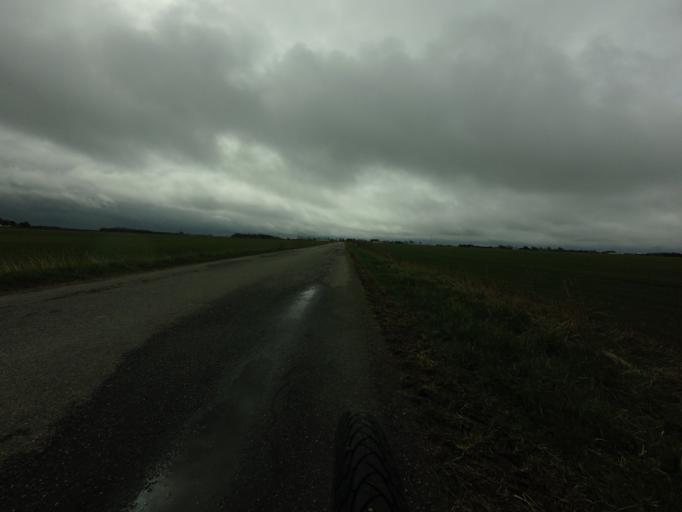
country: DK
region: North Denmark
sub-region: Hjorring Kommune
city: Vra
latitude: 57.3743
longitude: 9.8388
